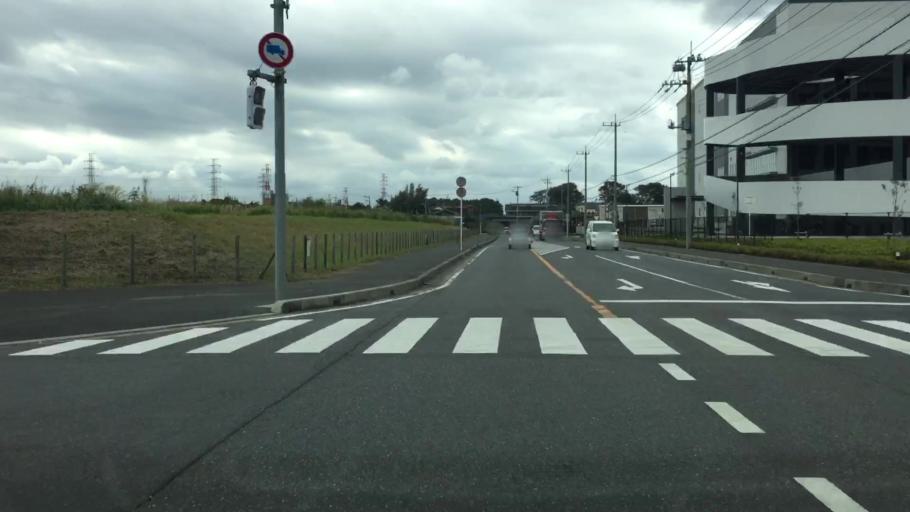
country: JP
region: Chiba
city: Shiroi
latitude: 35.8146
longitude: 140.1335
